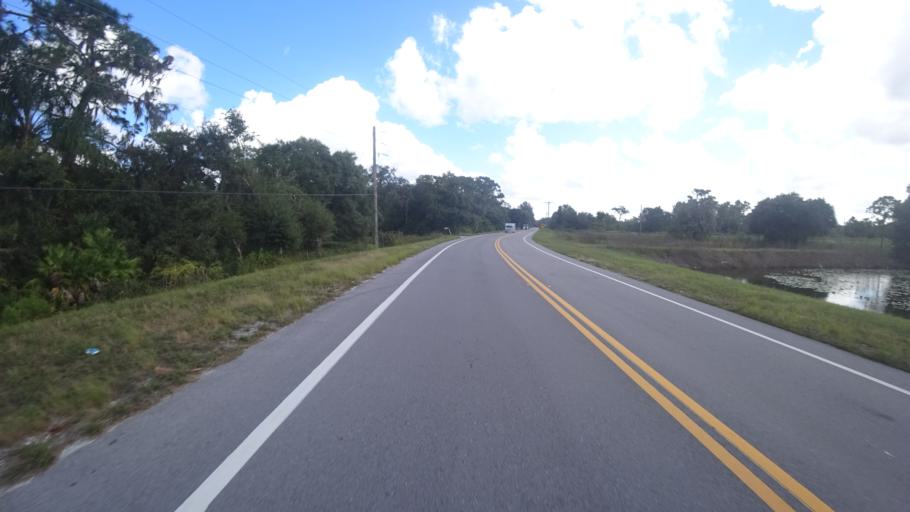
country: US
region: Florida
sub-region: Sarasota County
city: Lake Sarasota
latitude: 27.3681
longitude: -82.1455
